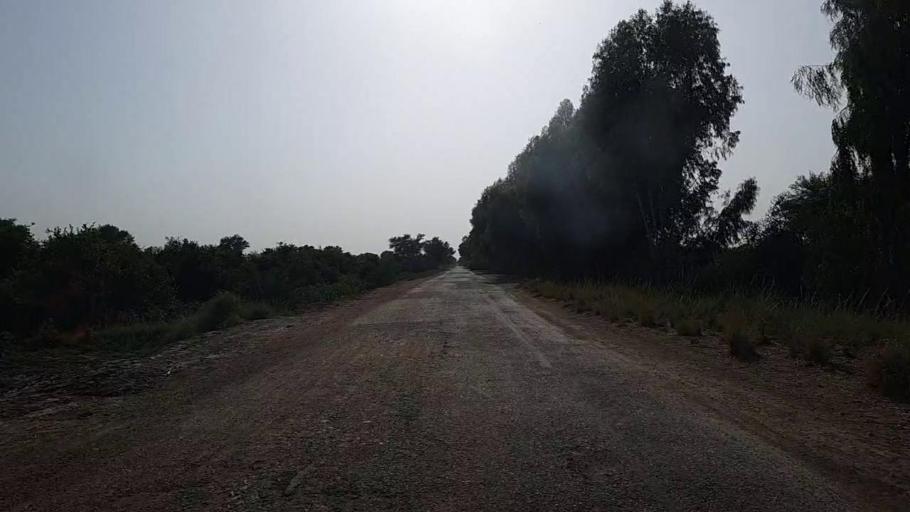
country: PK
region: Sindh
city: Pad Idan
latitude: 26.8532
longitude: 68.3290
